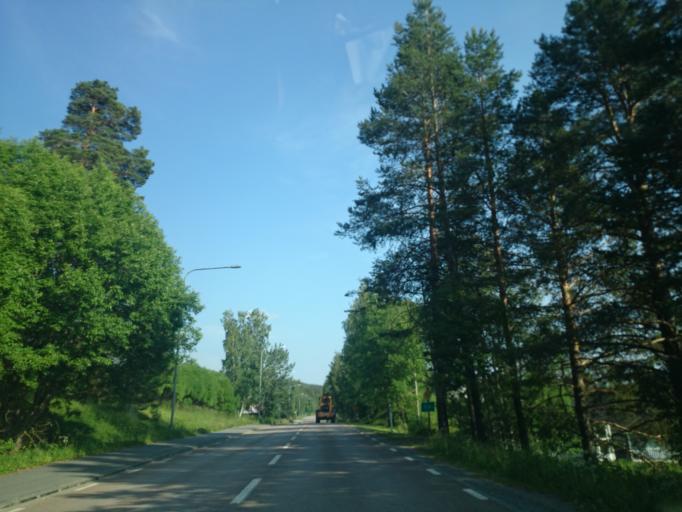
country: SE
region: Jaemtland
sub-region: OEstersunds Kommun
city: Brunflo
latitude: 62.9574
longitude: 15.0378
